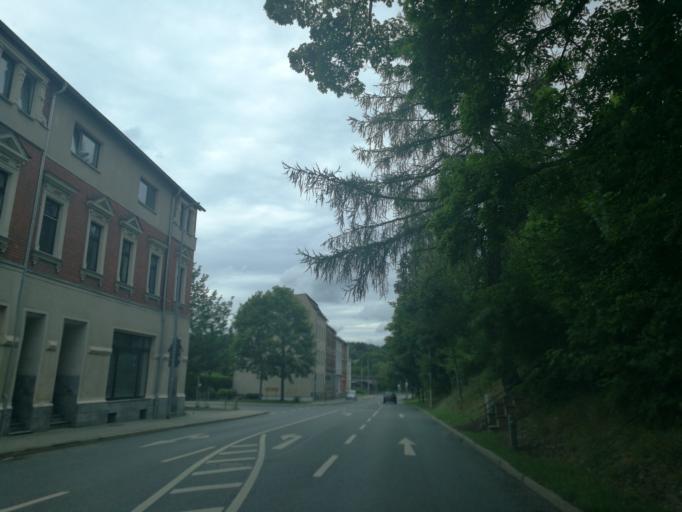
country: DE
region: Saxony
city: Adorf
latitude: 50.3198
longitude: 12.2638
